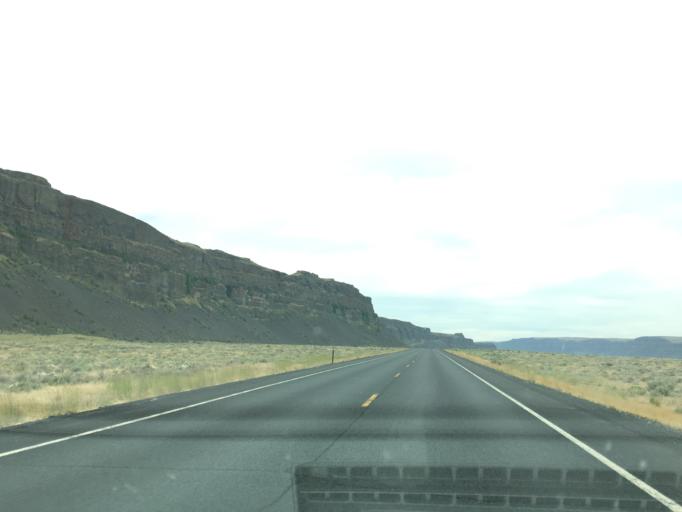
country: US
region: Washington
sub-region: Okanogan County
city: Coulee Dam
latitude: 47.7739
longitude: -119.2054
